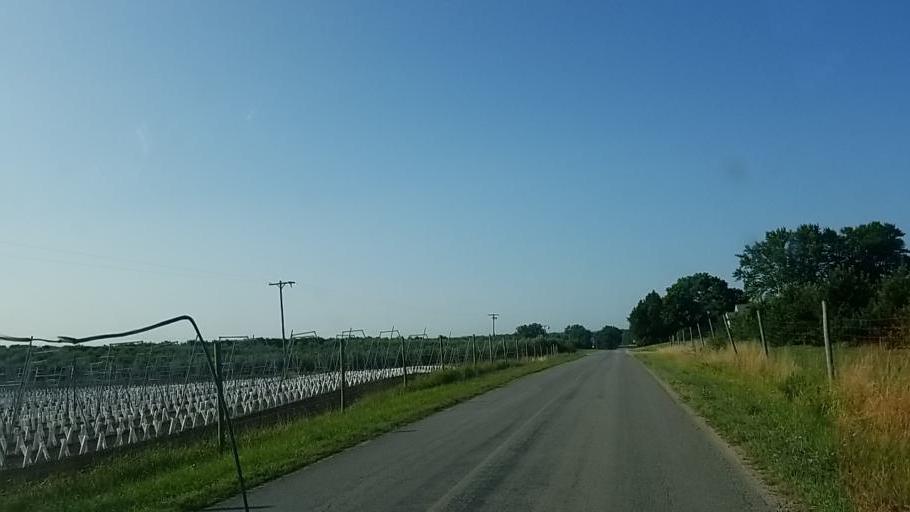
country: US
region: Michigan
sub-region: Newaygo County
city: Newaygo
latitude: 43.3595
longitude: -85.8208
